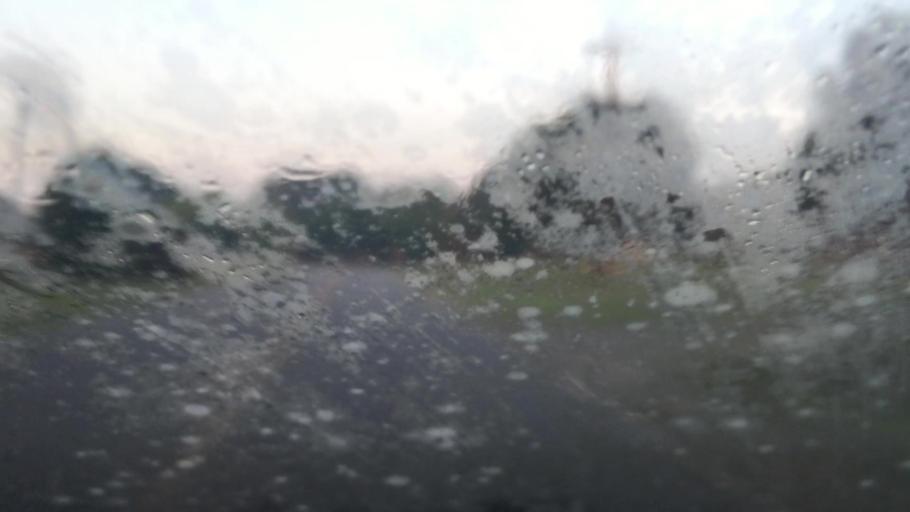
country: US
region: North Carolina
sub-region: Rockingham County
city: Reidsville
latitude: 36.3322
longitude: -79.6155
